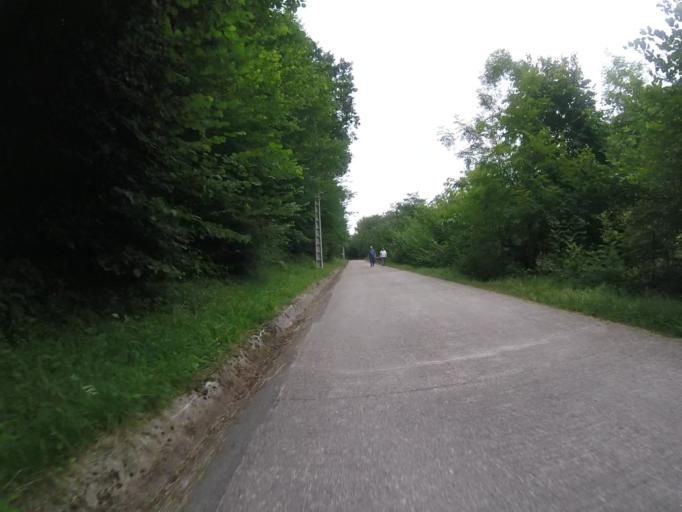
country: ES
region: Navarre
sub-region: Provincia de Navarra
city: Doneztebe
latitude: 43.1444
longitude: -1.6688
